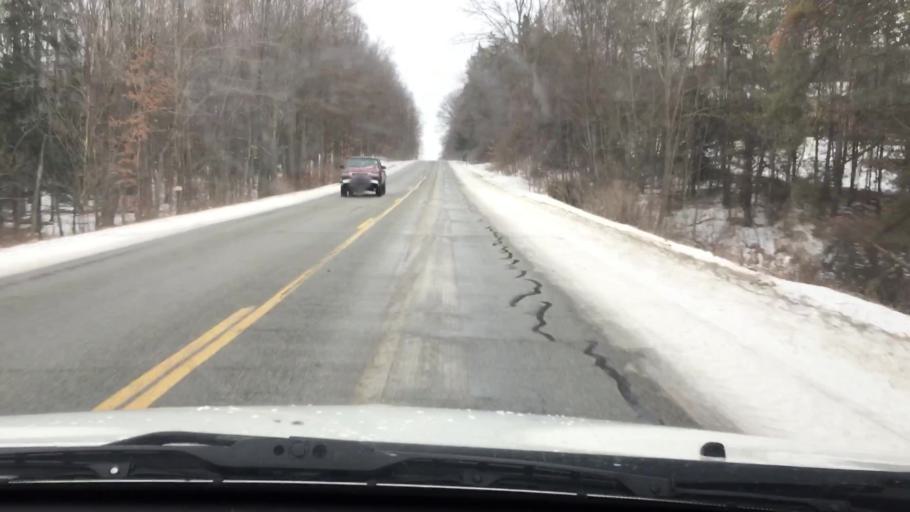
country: US
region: Michigan
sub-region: Wexford County
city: Cadillac
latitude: 44.1857
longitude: -85.4056
